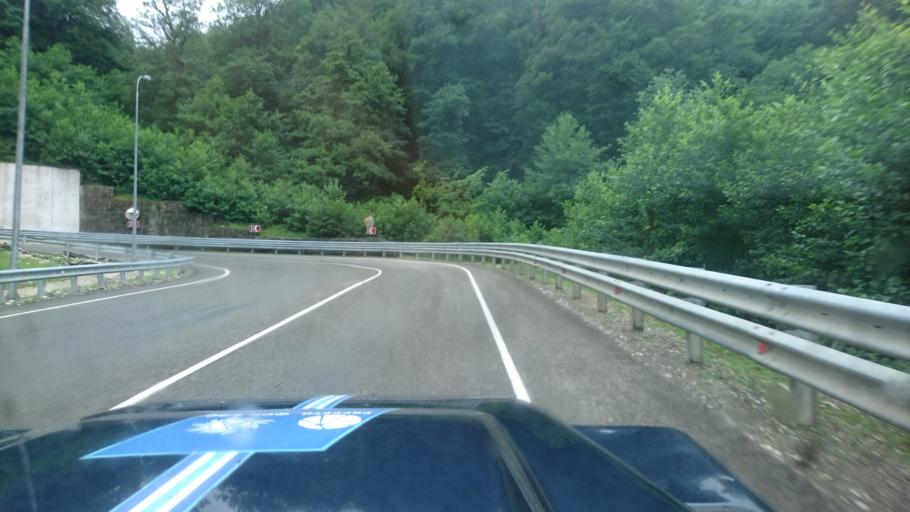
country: RU
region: Krasnodarskiy
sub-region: Sochi City
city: Krasnaya Polyana
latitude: 43.6720
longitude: 40.2857
